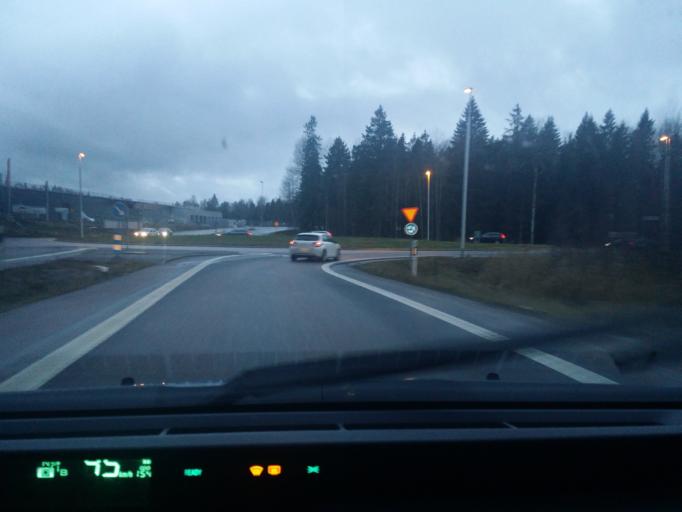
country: SE
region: Soedermanland
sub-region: Eskilstuna Kommun
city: Hallbybrunn
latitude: 59.4091
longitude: 16.3726
